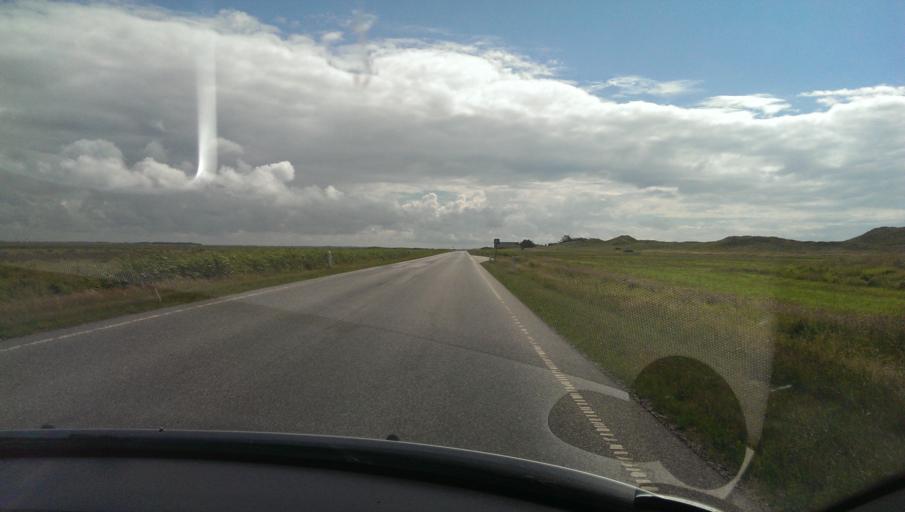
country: DK
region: Central Jutland
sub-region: Ringkobing-Skjern Kommune
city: Ringkobing
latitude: 56.2230
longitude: 8.1398
